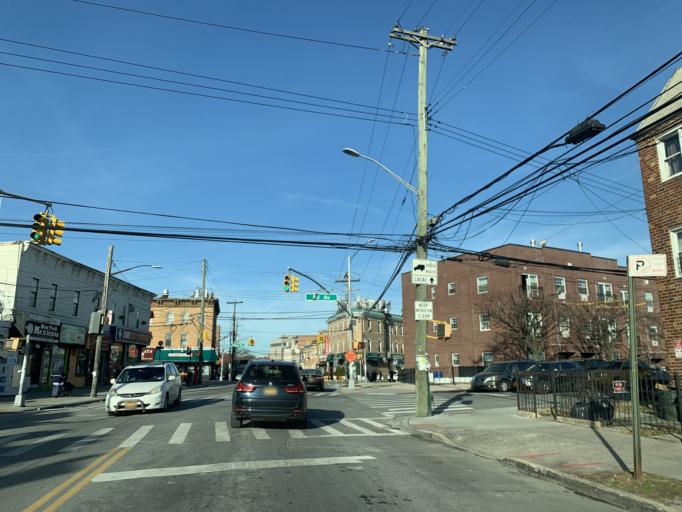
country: US
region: New York
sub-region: Queens County
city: Borough of Queens
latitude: 40.7415
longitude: -73.8675
